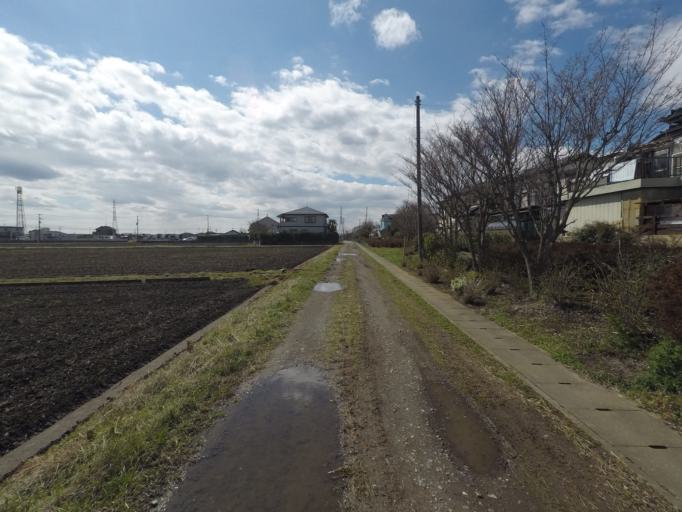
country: JP
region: Ibaraki
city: Fujishiro
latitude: 35.9370
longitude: 140.1257
